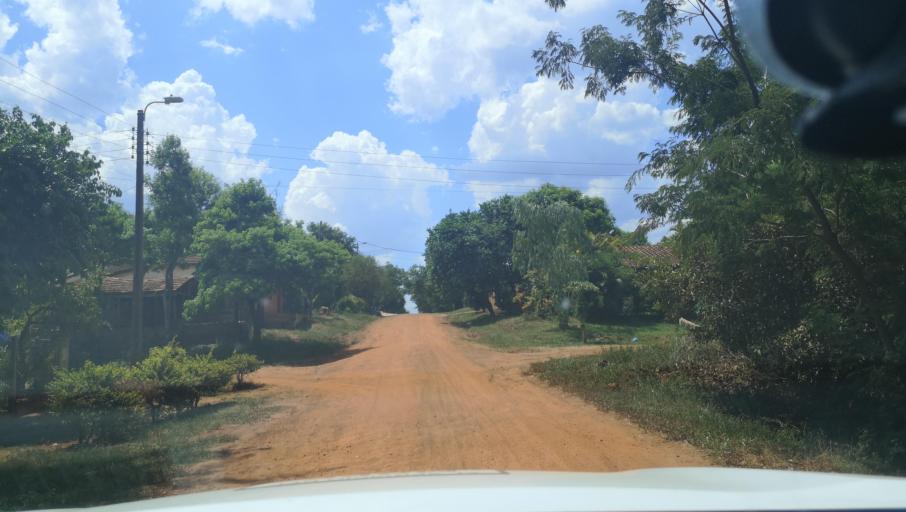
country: PY
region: Itapua
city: Carmen del Parana
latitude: -27.1706
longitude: -56.2462
